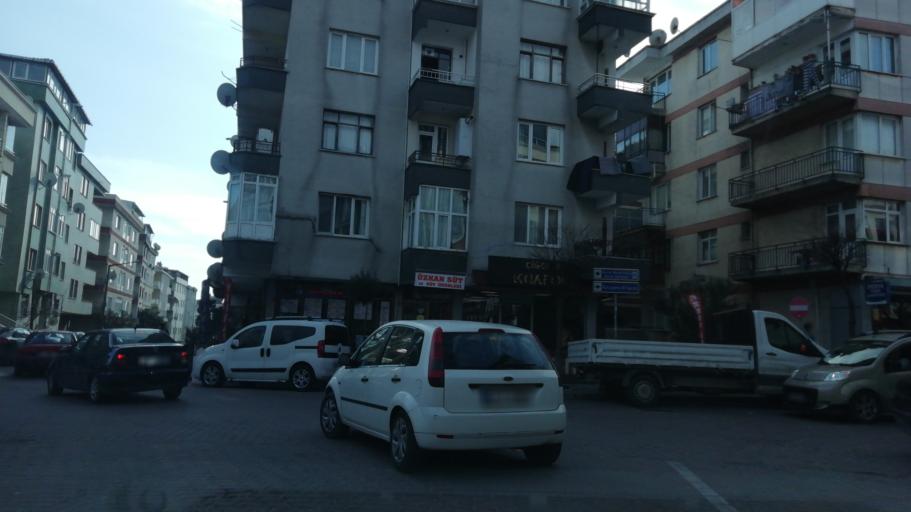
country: TR
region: Istanbul
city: Yakuplu
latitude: 40.9811
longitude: 28.7275
